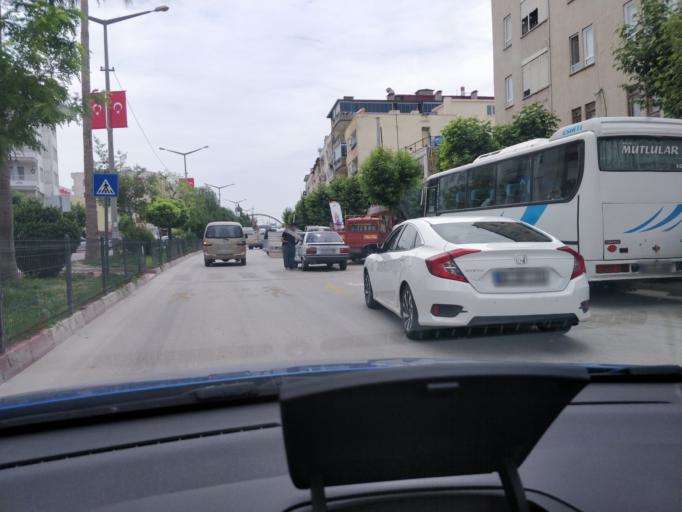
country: TR
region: Mersin
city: Mut
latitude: 36.6444
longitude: 33.4384
